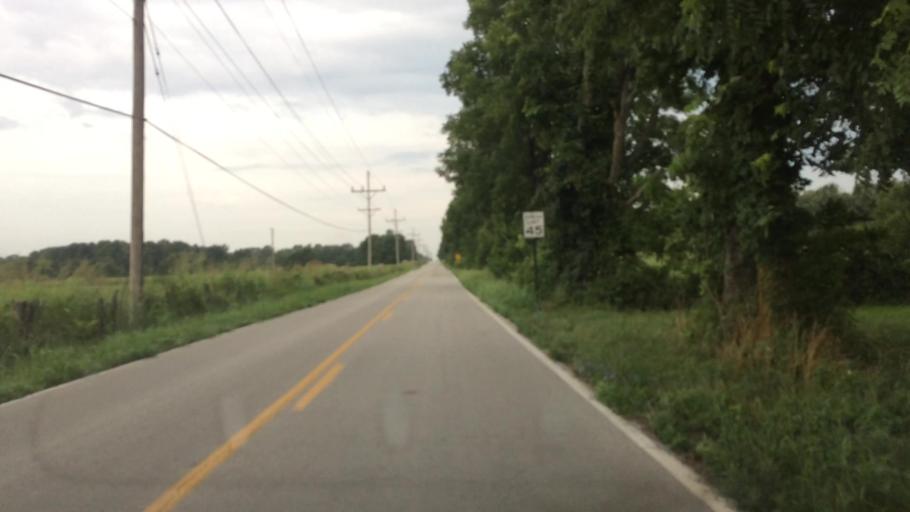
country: US
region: Missouri
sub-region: Greene County
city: Strafford
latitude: 37.2710
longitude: -93.1370
